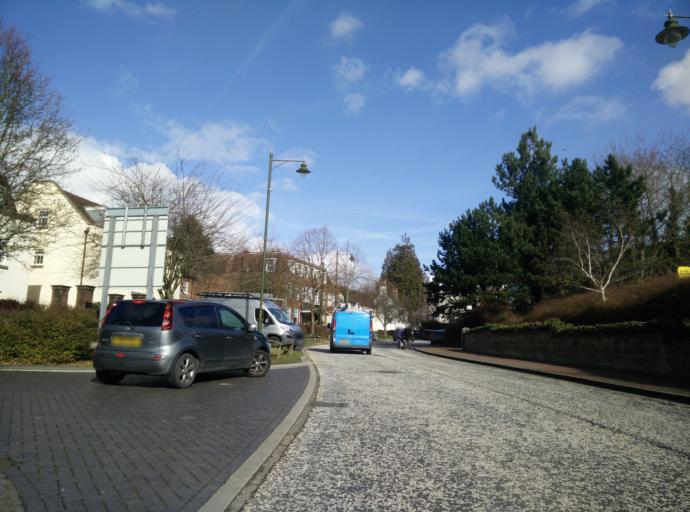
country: GB
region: England
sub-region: West Sussex
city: Horsham
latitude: 51.0619
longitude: -0.3340
